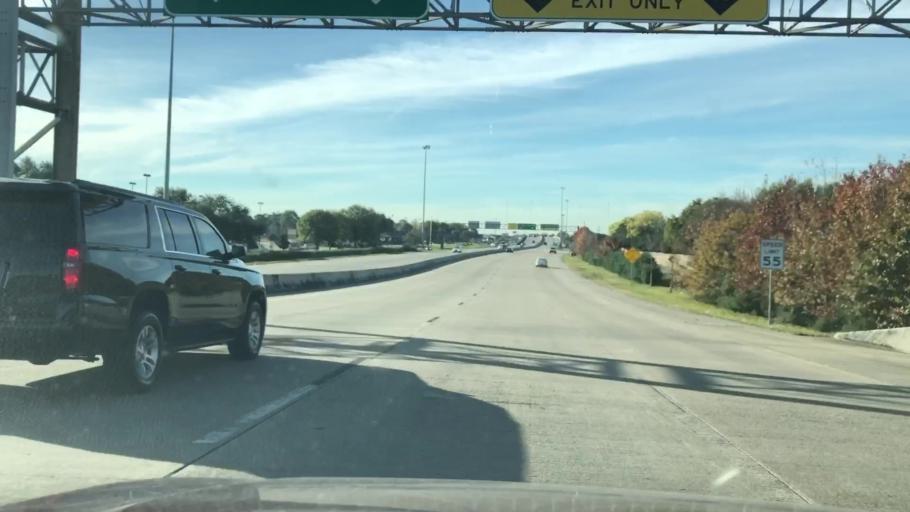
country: US
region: Texas
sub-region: Harris County
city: Bellaire
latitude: 29.6757
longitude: -95.4599
